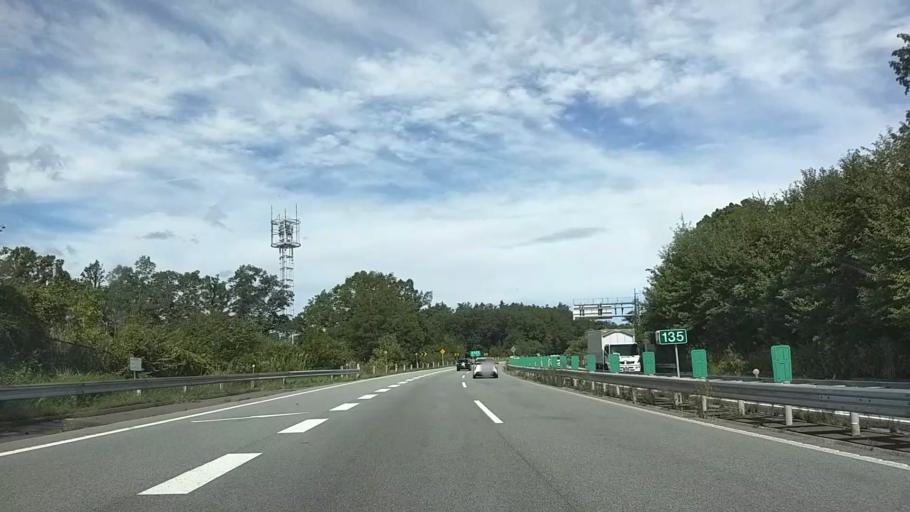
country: JP
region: Yamanashi
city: Nirasaki
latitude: 35.7933
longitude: 138.3994
